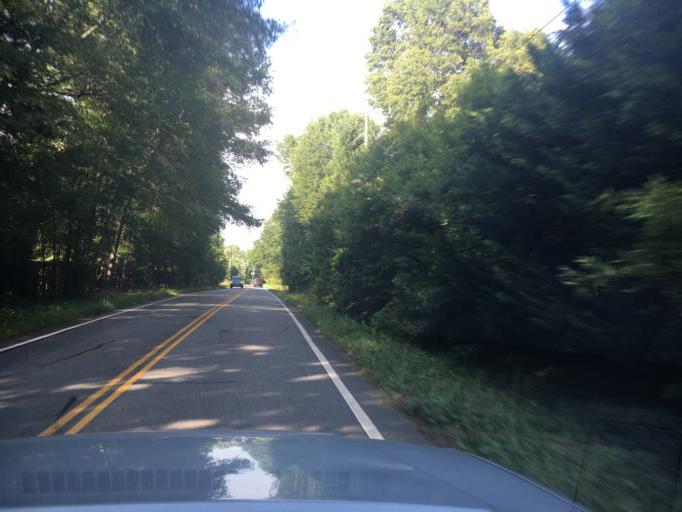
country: US
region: South Carolina
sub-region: Greenville County
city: Five Forks
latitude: 34.7865
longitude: -82.2403
